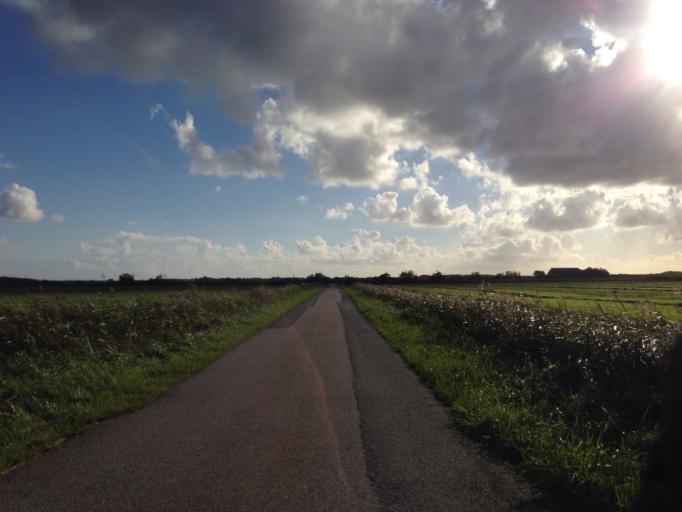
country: DE
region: Schleswig-Holstein
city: Oldsum
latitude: 54.7260
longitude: 8.4732
